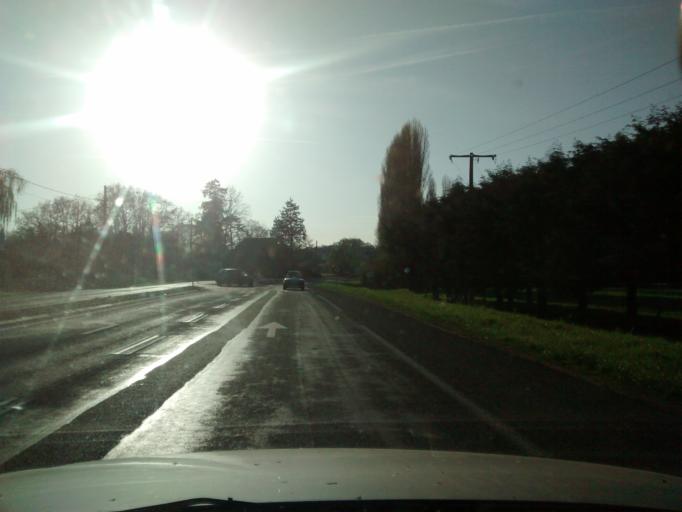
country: FR
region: Pays de la Loire
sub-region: Departement de la Sarthe
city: Change
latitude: 48.0121
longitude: 0.2785
